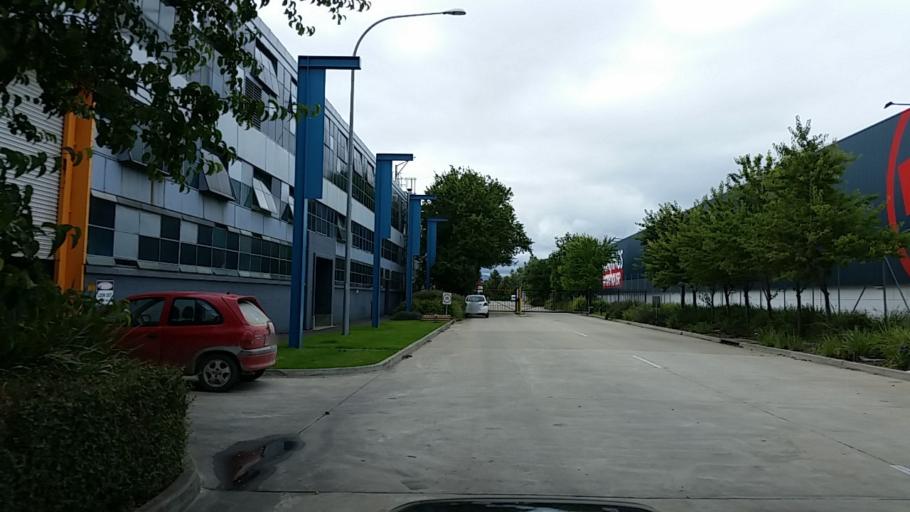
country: AU
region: South Australia
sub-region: Charles Sturt
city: Albert Park
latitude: -34.8741
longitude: 138.5293
